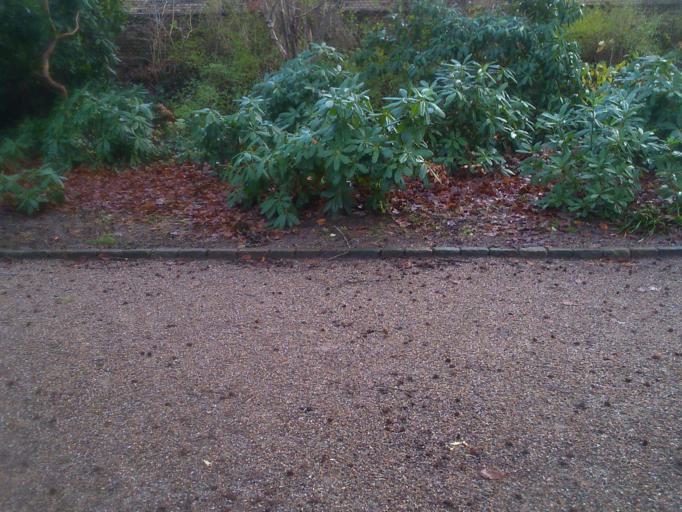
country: DK
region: Central Jutland
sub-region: Ikast-Brande Kommune
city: Ikast
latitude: 56.1410
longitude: 9.1646
